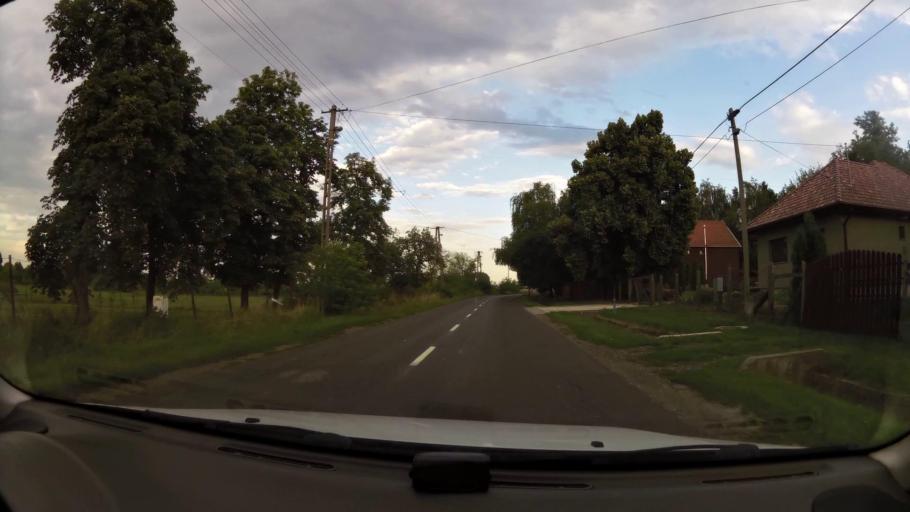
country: HU
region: Pest
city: Tapiobicske
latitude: 47.3560
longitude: 19.6971
